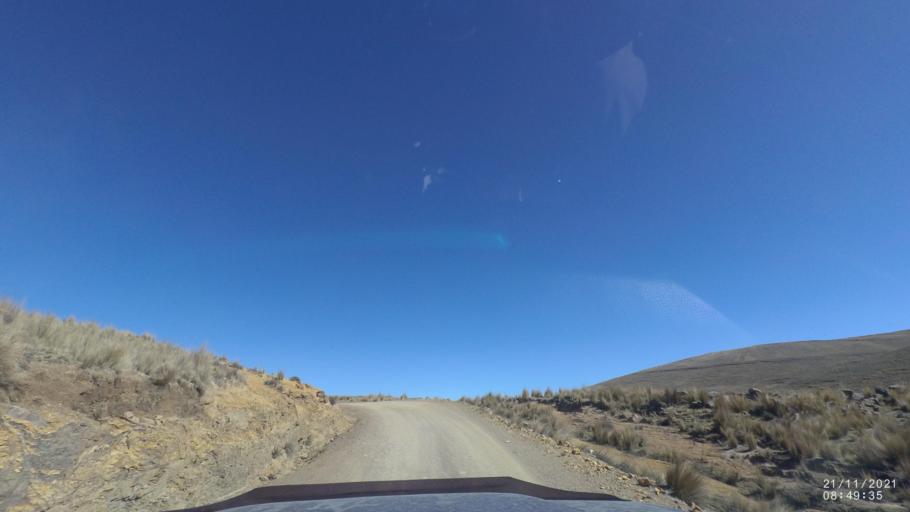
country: BO
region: Cochabamba
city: Cochabamba
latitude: -17.2237
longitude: -66.2323
